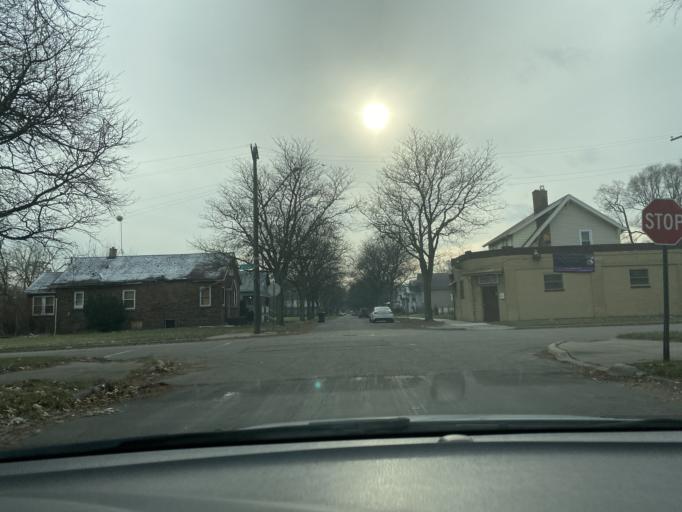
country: US
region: Michigan
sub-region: Wayne County
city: Highland Park
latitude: 42.3712
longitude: -83.1311
